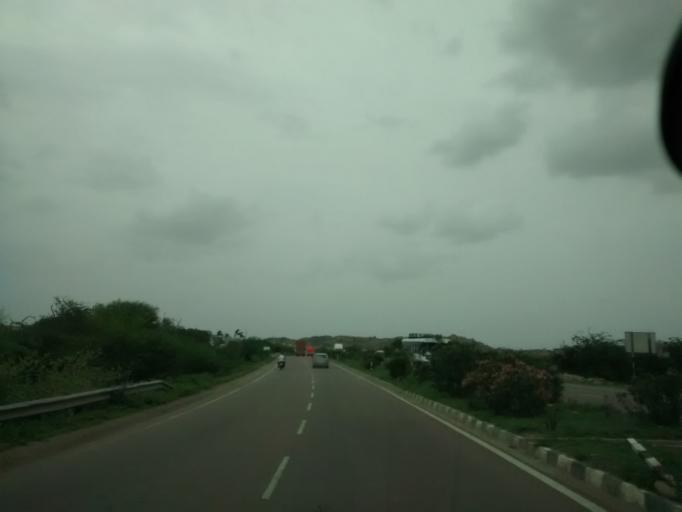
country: IN
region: Andhra Pradesh
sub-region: Kurnool
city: Ramapuram
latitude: 15.1721
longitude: 77.6834
